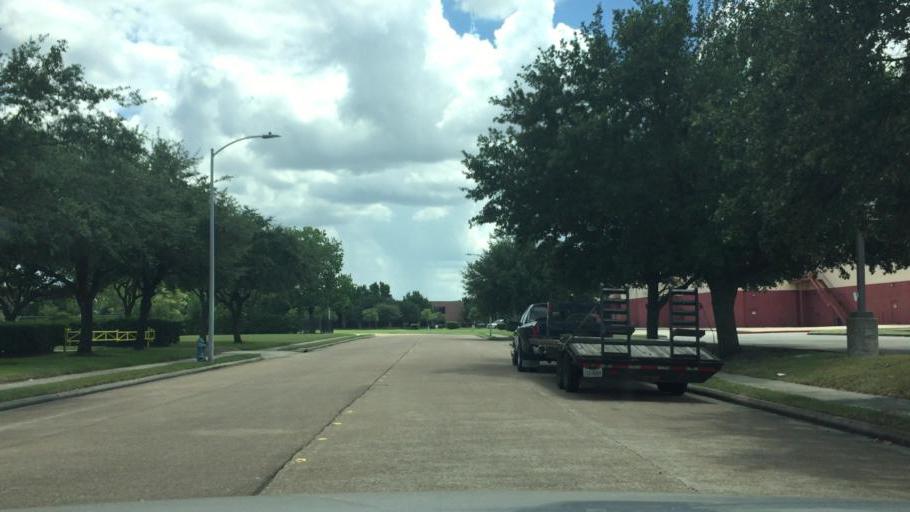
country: US
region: Texas
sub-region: Harris County
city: Hudson
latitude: 29.8480
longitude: -95.4973
